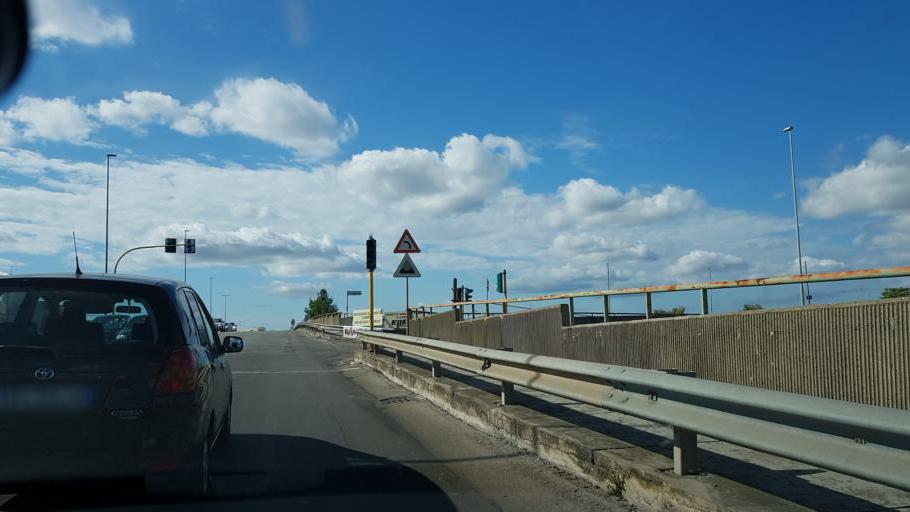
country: IT
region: Apulia
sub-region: Provincia di Lecce
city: Lecce
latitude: 40.3550
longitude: 18.1519
